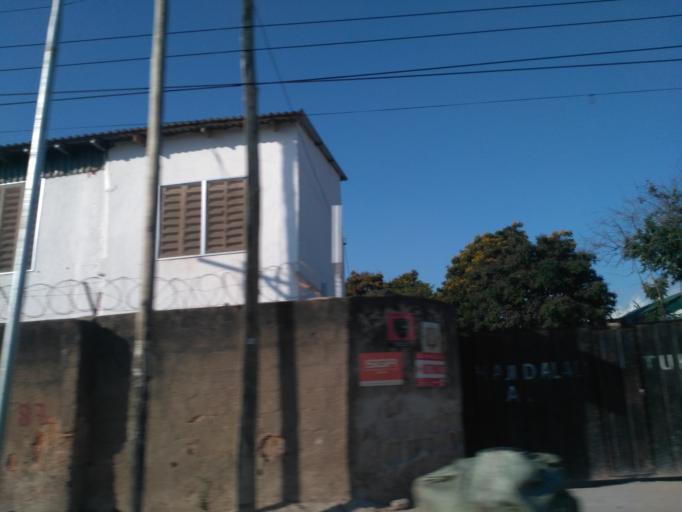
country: TZ
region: Dar es Salaam
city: Magomeni
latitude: -6.7628
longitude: 39.2428
